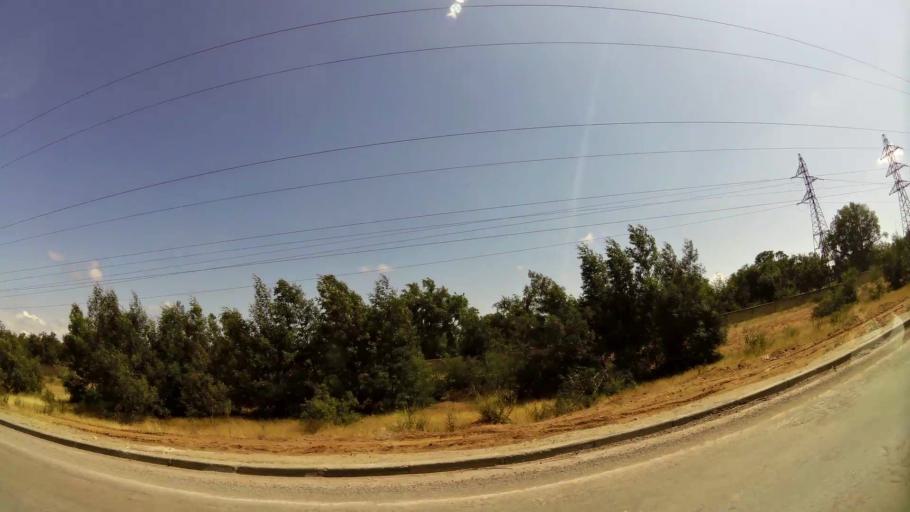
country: MA
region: Gharb-Chrarda-Beni Hssen
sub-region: Kenitra Province
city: Kenitra
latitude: 34.2366
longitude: -6.5686
